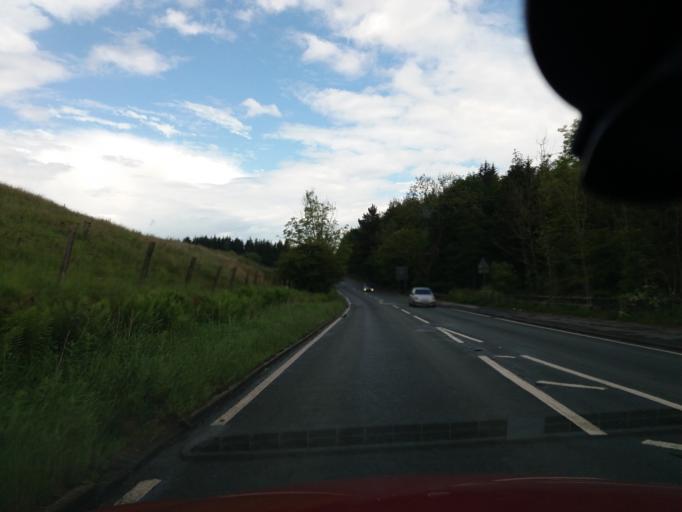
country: GB
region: England
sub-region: Blackburn with Darwen
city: Darwen
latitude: 53.6564
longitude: -2.4524
